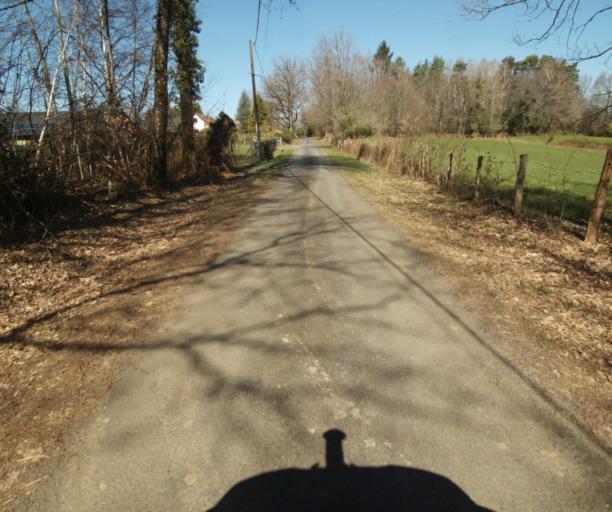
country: FR
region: Limousin
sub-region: Departement de la Correze
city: Saint-Clement
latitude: 45.3235
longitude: 1.6533
